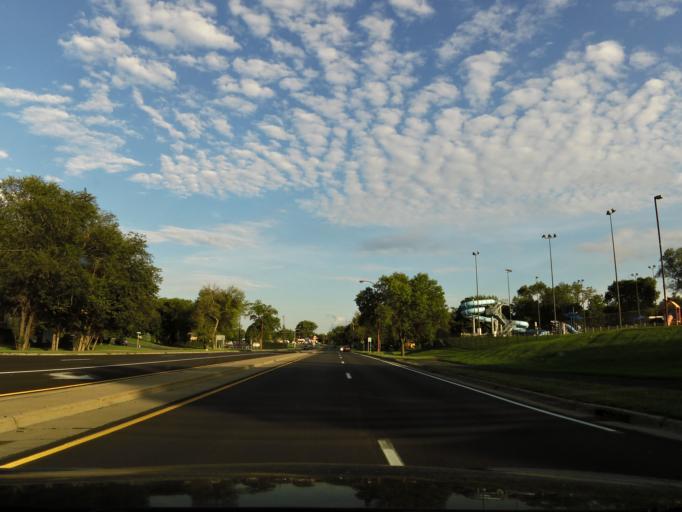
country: US
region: Minnesota
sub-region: Dakota County
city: Hastings
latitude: 44.7375
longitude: -92.8594
